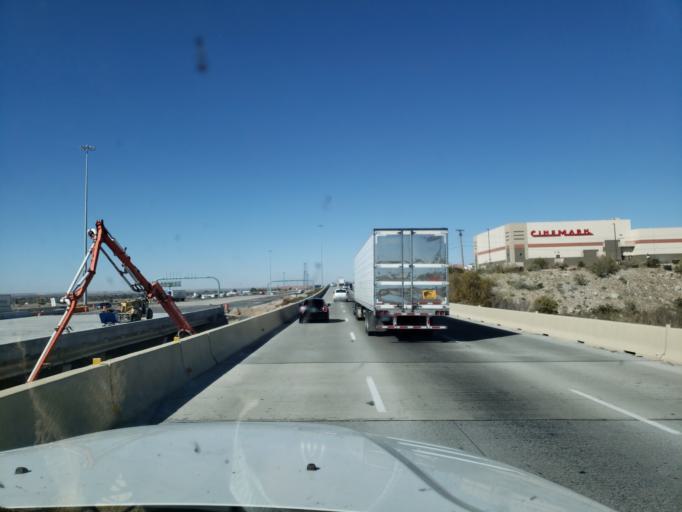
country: US
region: New Mexico
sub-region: Dona Ana County
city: Sunland Park
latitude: 31.8301
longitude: -106.5638
